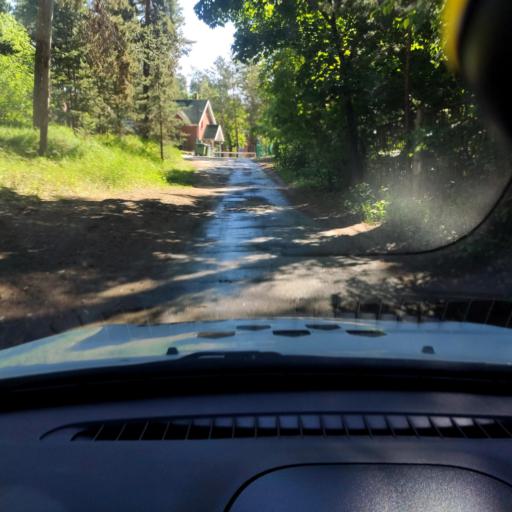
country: RU
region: Samara
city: Tol'yatti
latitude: 53.4685
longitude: 49.3899
